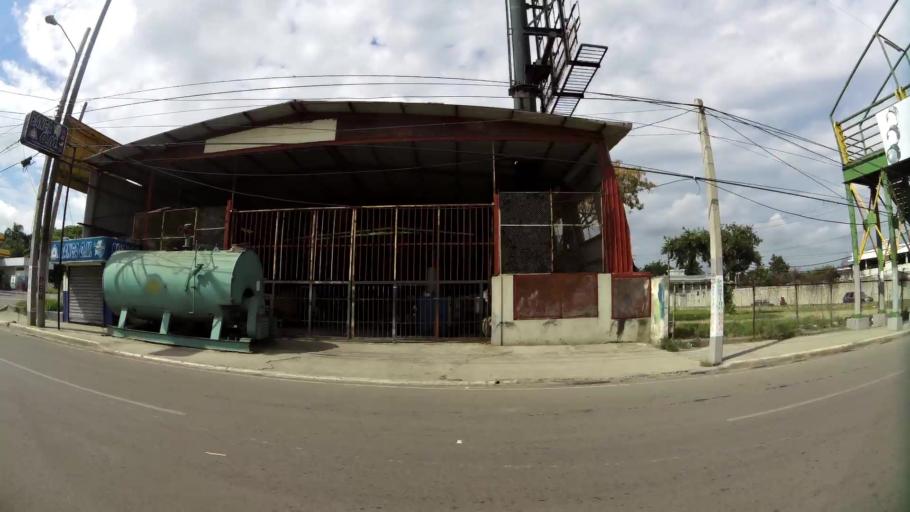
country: DO
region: Santiago
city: Santiago de los Caballeros
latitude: 19.4831
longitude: -70.7292
